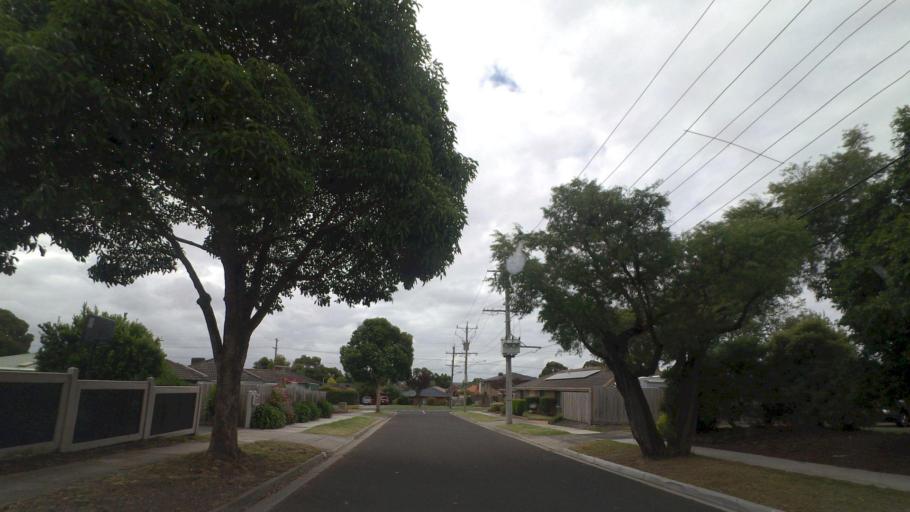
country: AU
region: Victoria
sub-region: Knox
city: Wantirna South
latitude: -37.8897
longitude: 145.2204
